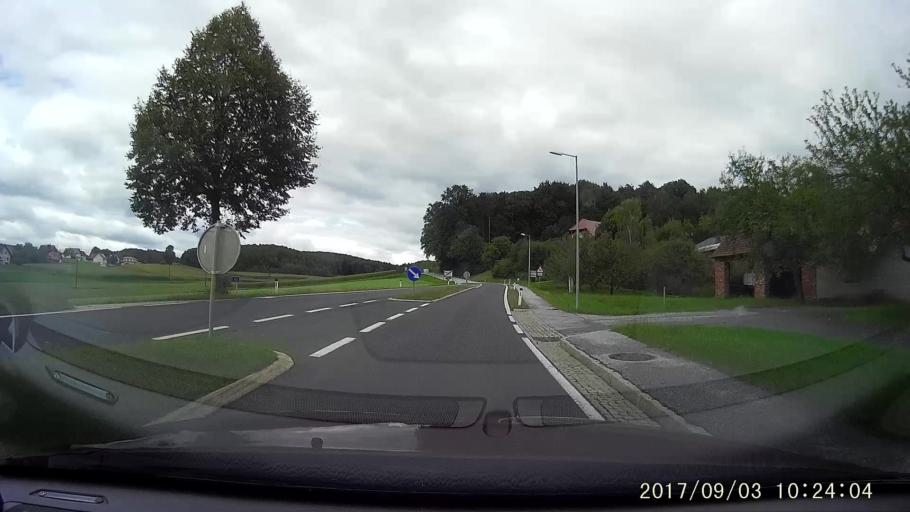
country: AT
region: Styria
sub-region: Politischer Bezirk Hartberg-Fuerstenfeld
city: Ilz
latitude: 47.0570
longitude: 15.9241
